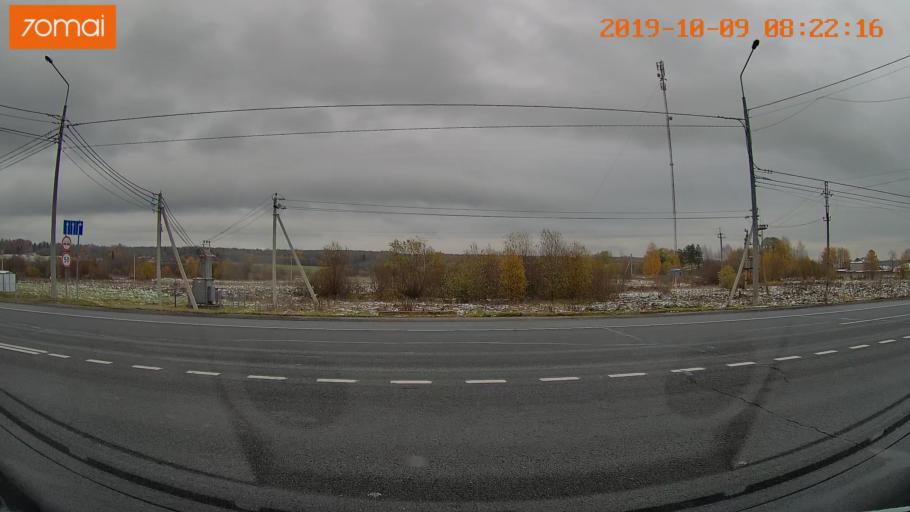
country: RU
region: Vologda
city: Gryazovets
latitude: 58.7419
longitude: 40.2885
